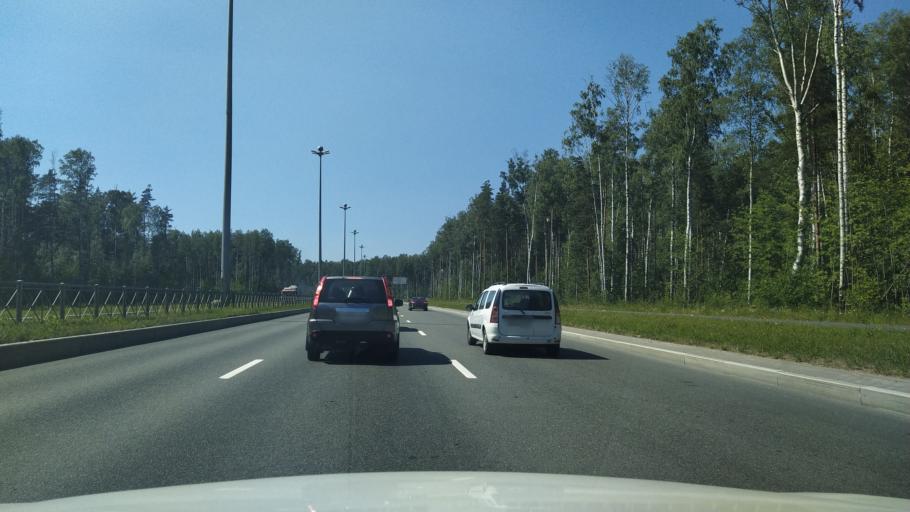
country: RU
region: St.-Petersburg
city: Pargolovo
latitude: 60.0597
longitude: 30.2562
